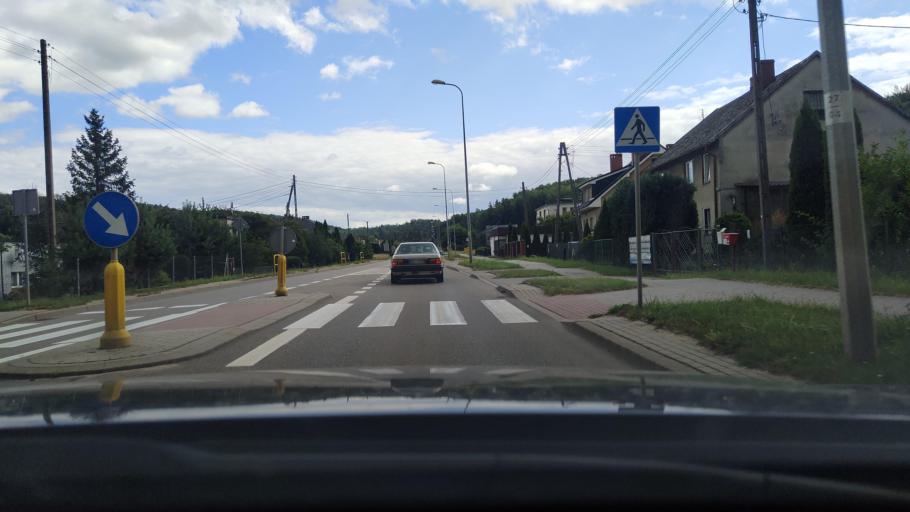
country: PL
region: Pomeranian Voivodeship
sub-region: Powiat wejherowski
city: Wejherowo
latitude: 54.5903
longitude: 18.2424
